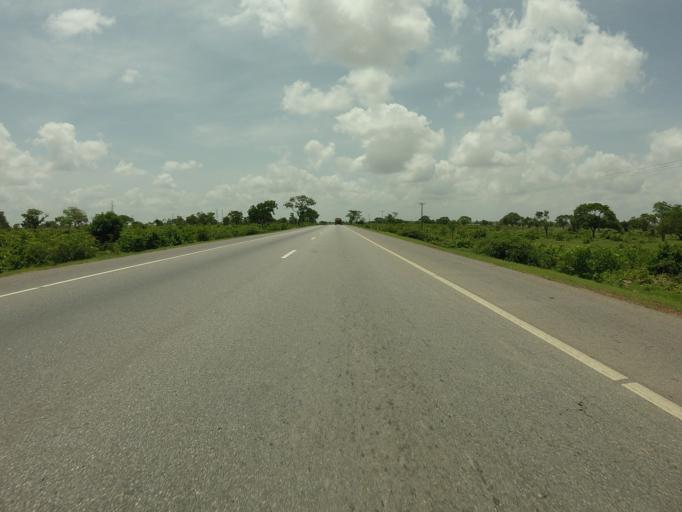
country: GH
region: Northern
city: Tamale
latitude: 9.3068
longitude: -0.9558
